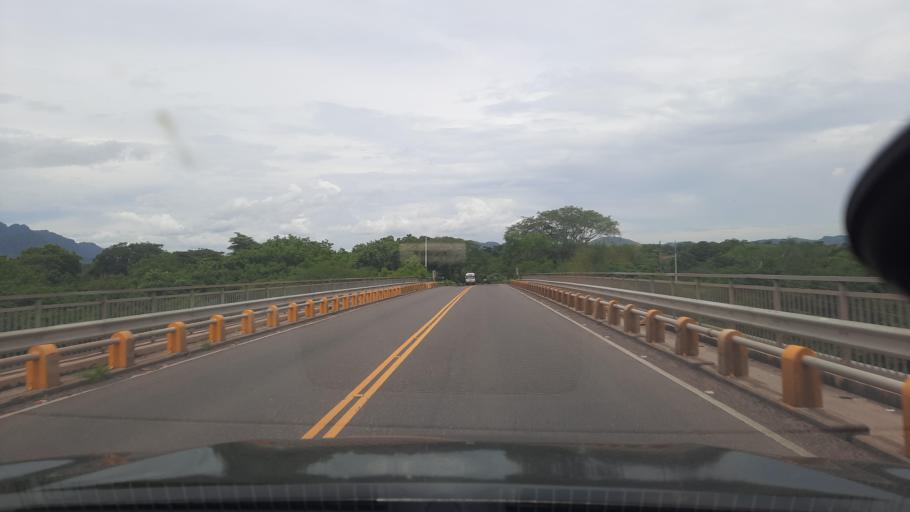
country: HN
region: Valle
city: Nacaome
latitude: 13.5359
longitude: -87.4644
